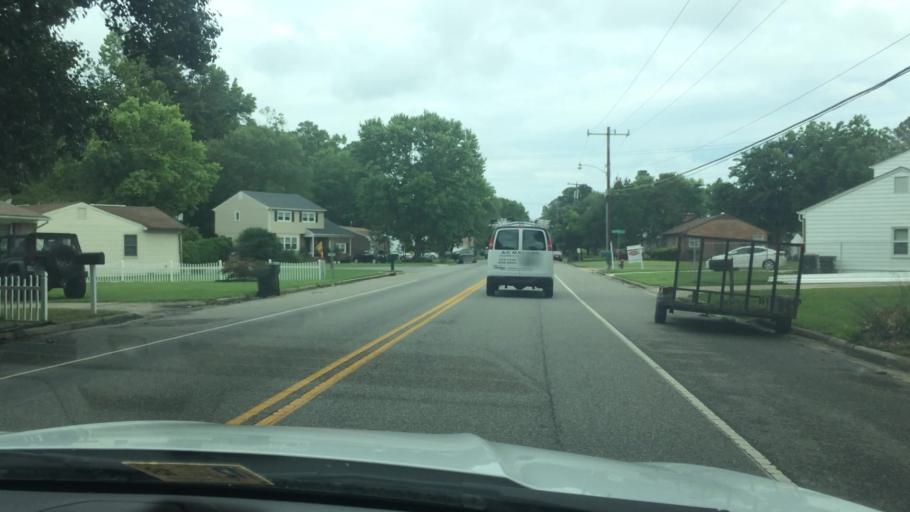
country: US
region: Virginia
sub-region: City of Williamsburg
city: Williamsburg
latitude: 37.2735
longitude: -76.6722
